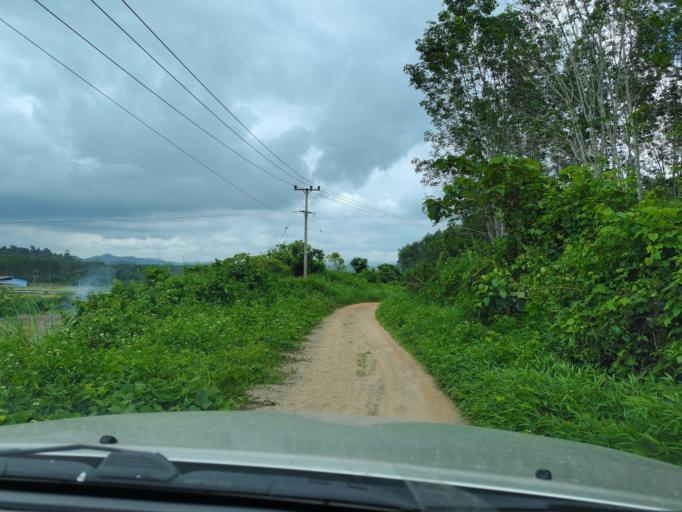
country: LA
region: Loungnamtha
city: Muang Long
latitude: 20.6973
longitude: 101.0386
